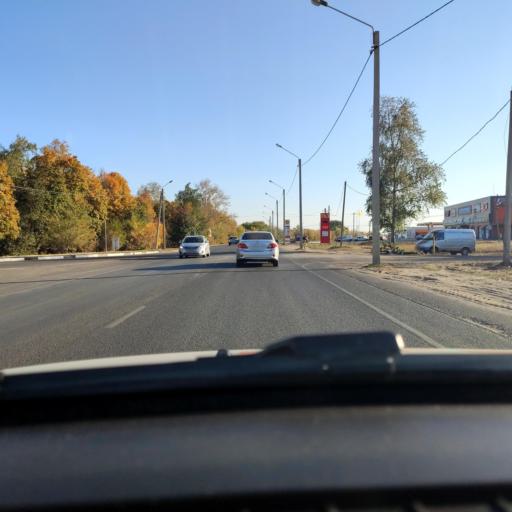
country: RU
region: Voronezj
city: Voronezh
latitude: 51.6171
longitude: 39.1777
